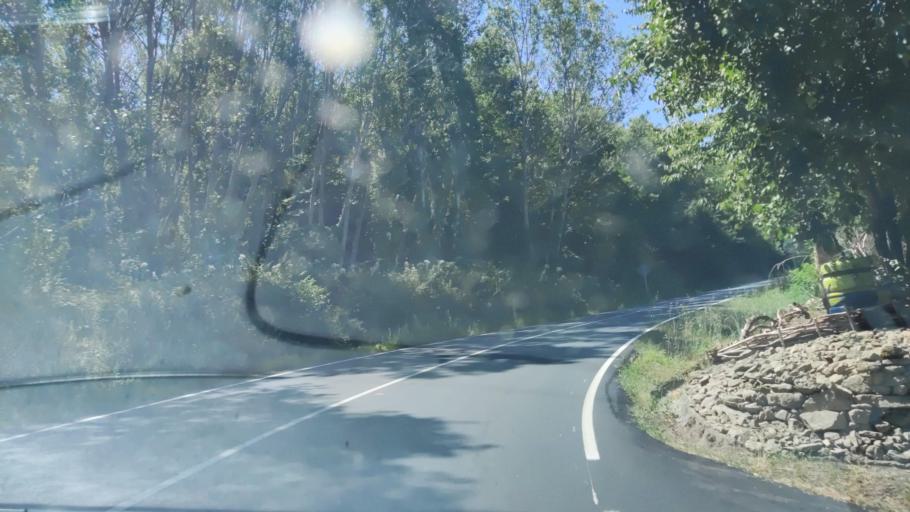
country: ES
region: Castille and Leon
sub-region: Provincia de Salamanca
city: Candelario
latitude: 40.3701
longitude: -5.7516
